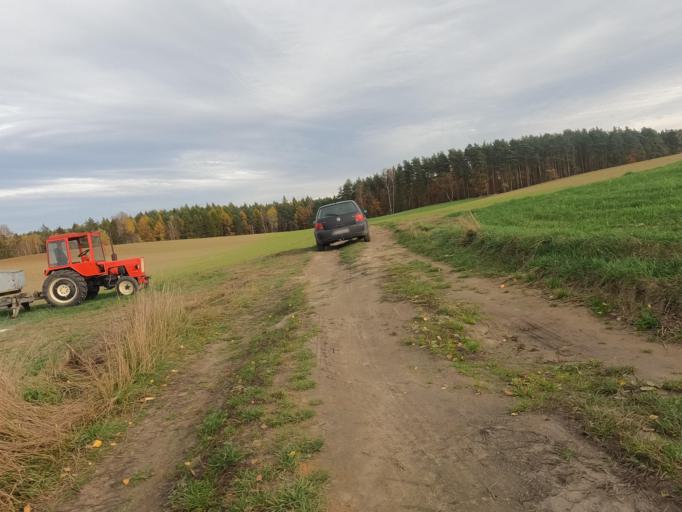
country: PL
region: Pomeranian Voivodeship
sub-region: Powiat starogardzki
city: Skarszewy
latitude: 54.0050
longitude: 18.4538
